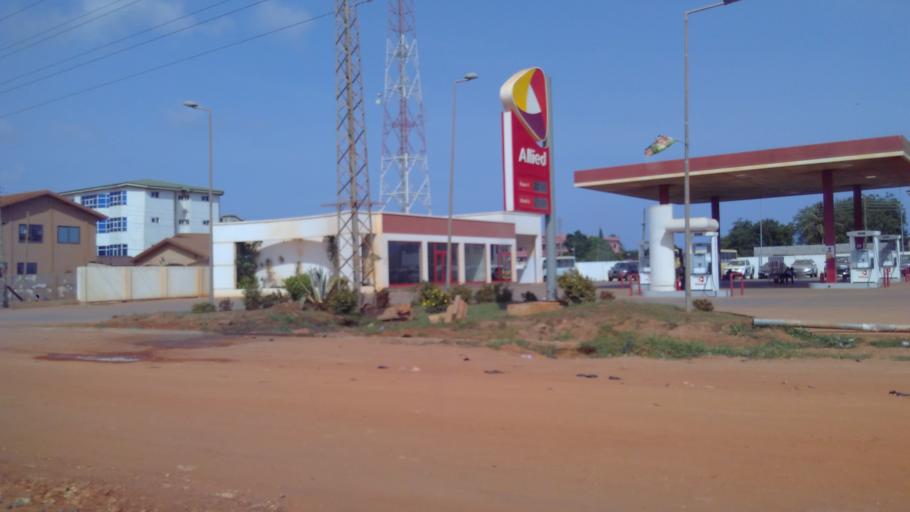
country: GH
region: Greater Accra
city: Nungua
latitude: 5.6292
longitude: -0.0668
